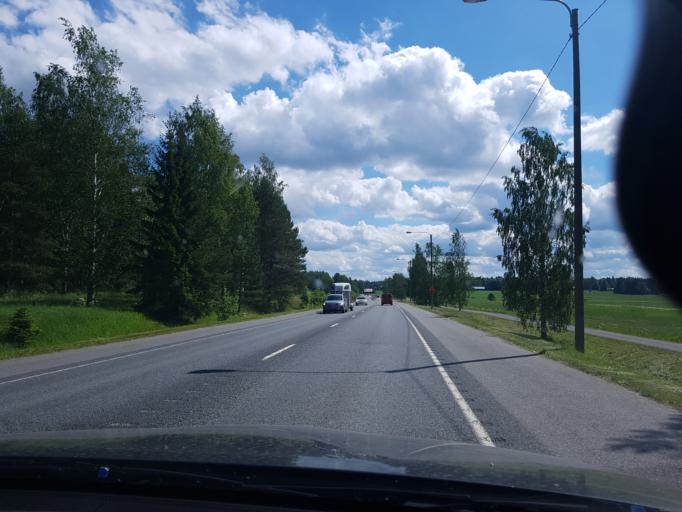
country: FI
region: Haeme
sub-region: Haemeenlinna
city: Parola
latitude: 61.0473
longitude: 24.3967
